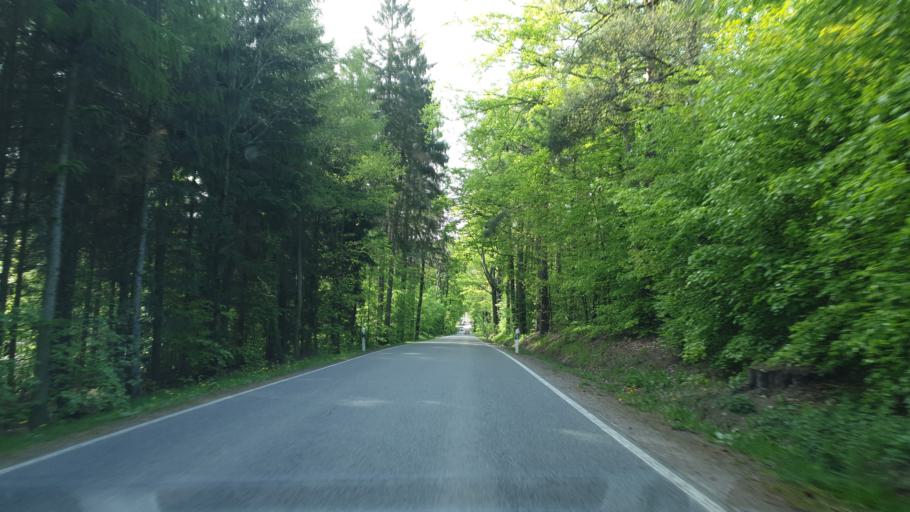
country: DE
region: Saxony
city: Lichtenstein
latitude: 50.7212
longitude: 12.6475
